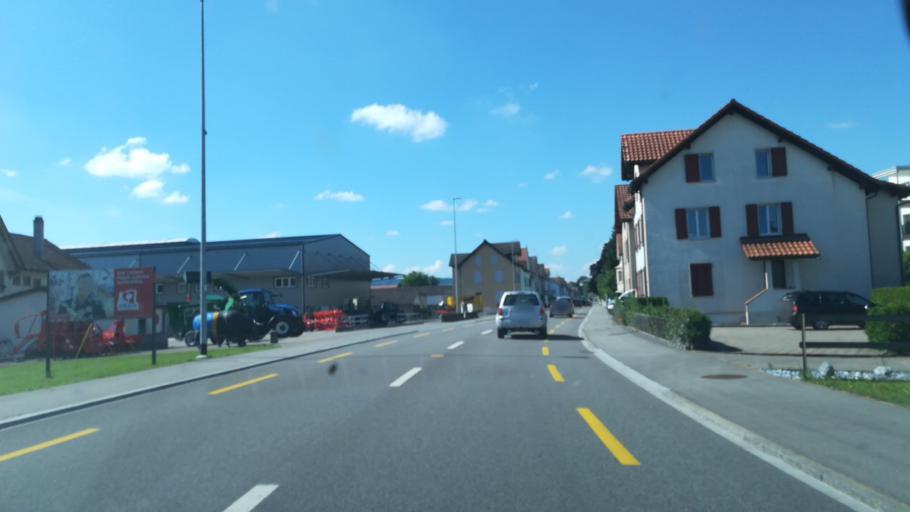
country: CH
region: Thurgau
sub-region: Weinfelden District
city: Sulgen
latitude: 47.5336
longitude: 9.1875
